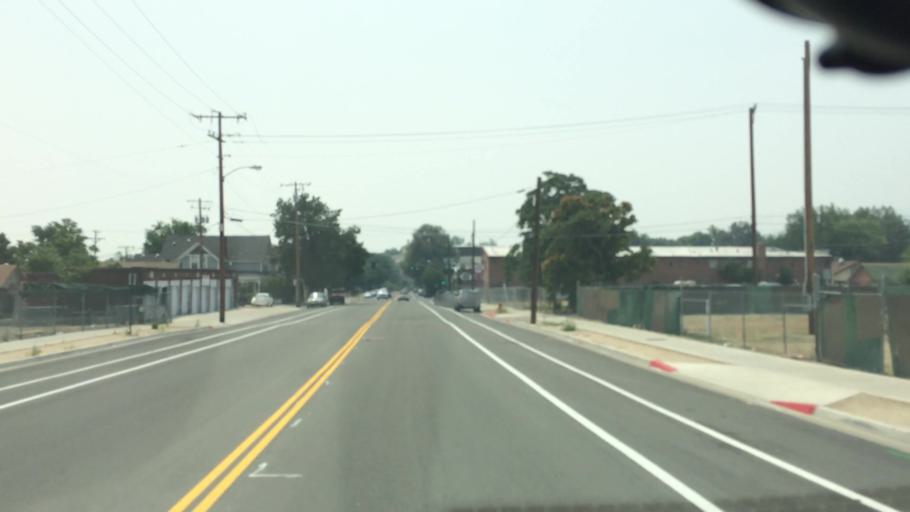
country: US
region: Nevada
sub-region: Washoe County
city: Reno
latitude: 39.5271
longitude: -119.8203
